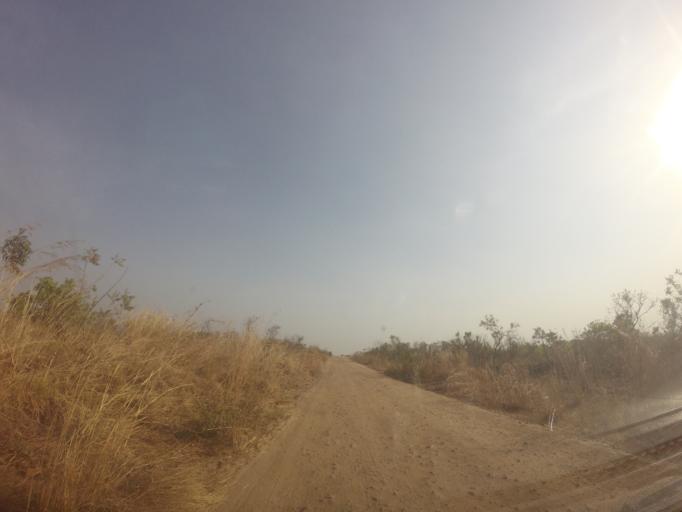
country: UG
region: Northern Region
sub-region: Maracha District
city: Maracha
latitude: 3.1149
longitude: 31.1567
